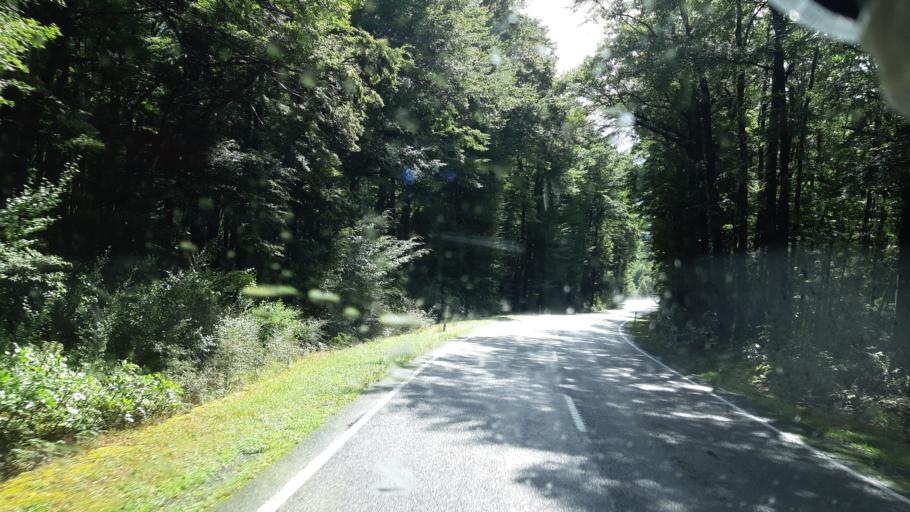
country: NZ
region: West Coast
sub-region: Buller District
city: Westport
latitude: -42.3743
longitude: 172.2704
